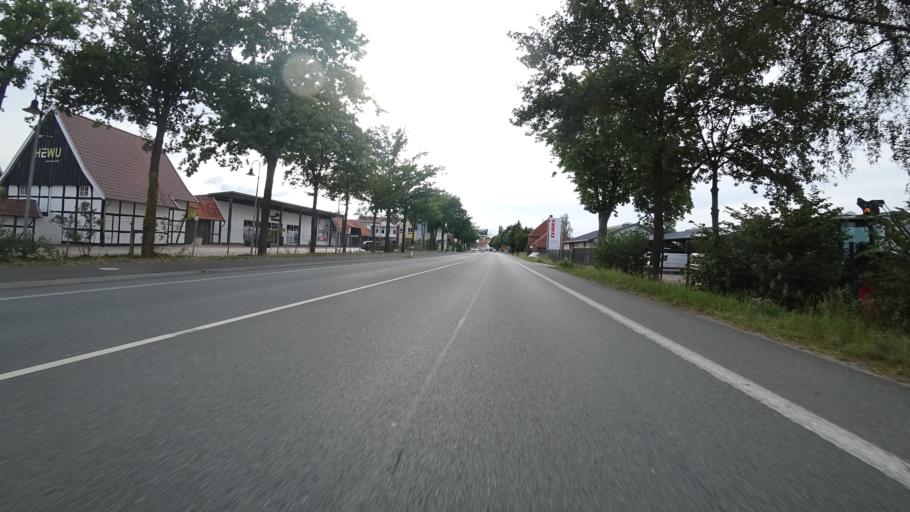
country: DE
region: North Rhine-Westphalia
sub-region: Regierungsbezirk Detmold
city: Harsewinkel
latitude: 51.9400
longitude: 8.2969
